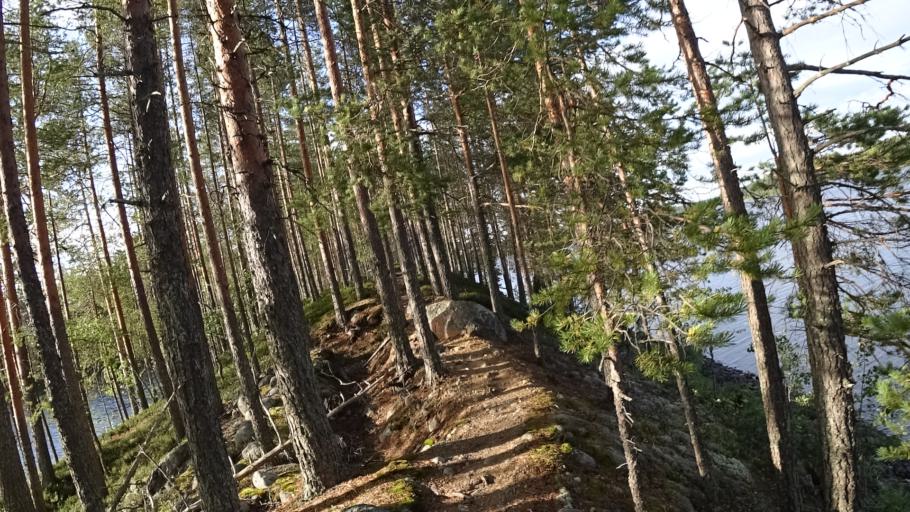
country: FI
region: North Karelia
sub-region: Joensuu
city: Ilomantsi
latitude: 62.5661
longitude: 31.1827
